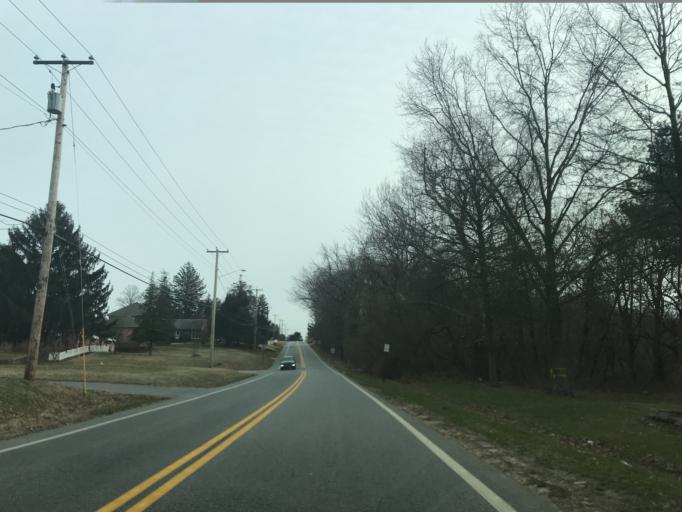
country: US
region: Maryland
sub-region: Cecil County
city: Elkton
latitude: 39.6063
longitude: -75.8186
